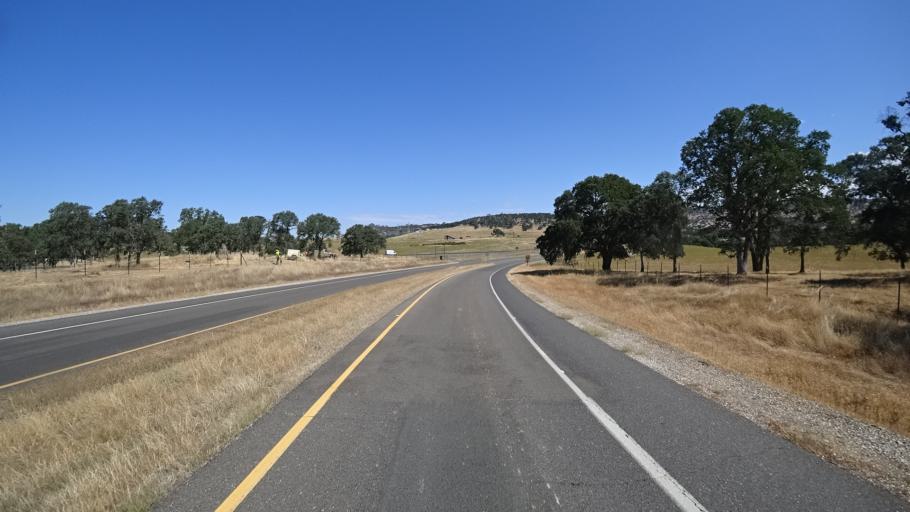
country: US
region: California
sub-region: Calaveras County
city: Copperopolis
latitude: 37.9693
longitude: -120.6576
